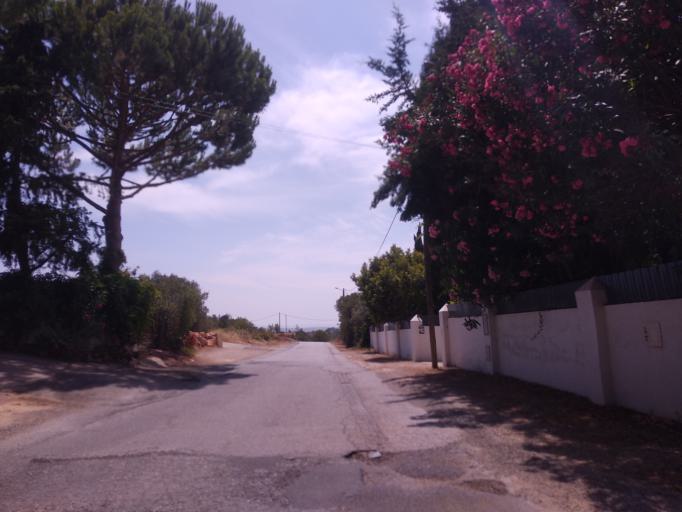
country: PT
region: Faro
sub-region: Faro
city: Santa Barbara de Nexe
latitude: 37.1089
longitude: -7.9493
